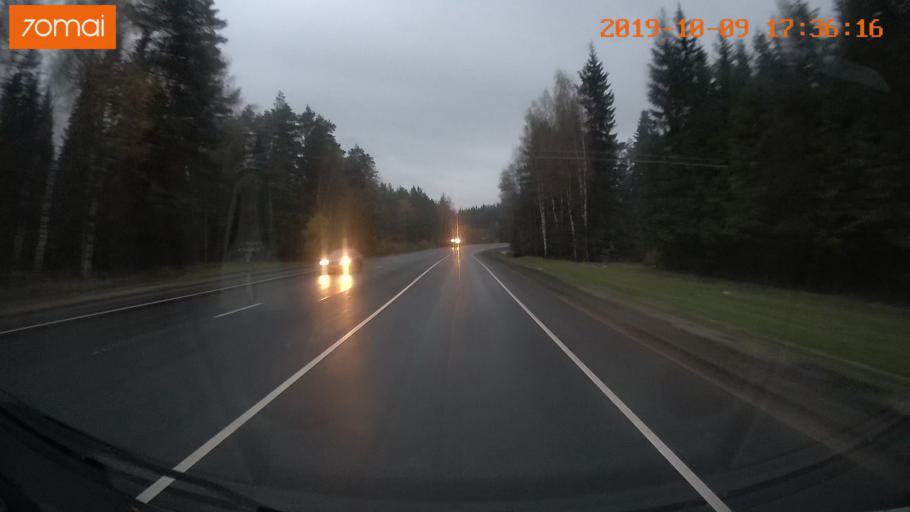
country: RU
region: Ivanovo
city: Bogorodskoye
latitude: 57.0808
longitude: 40.9979
